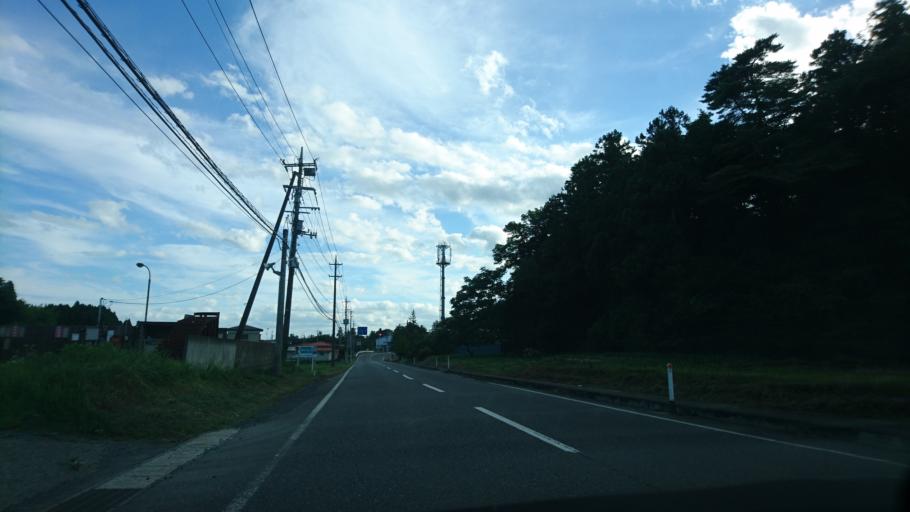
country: JP
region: Iwate
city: Ichinoseki
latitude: 38.8522
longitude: 141.1810
